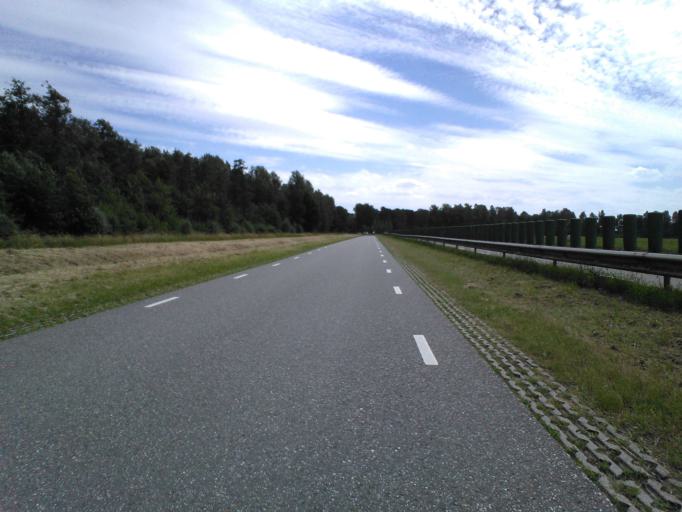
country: NL
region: South Holland
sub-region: Gemeente Papendrecht
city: Papendrecht
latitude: 51.8492
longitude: 4.7318
